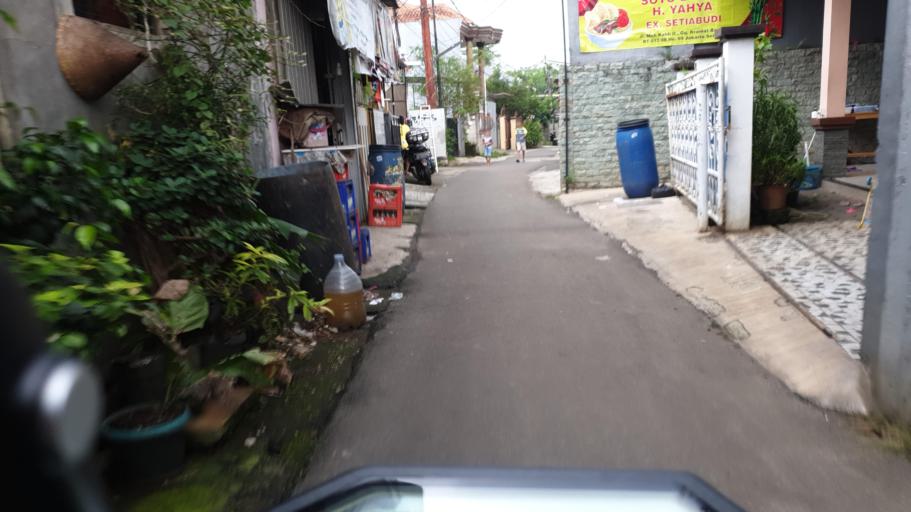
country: ID
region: West Java
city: Depok
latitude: -6.3409
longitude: 106.8211
